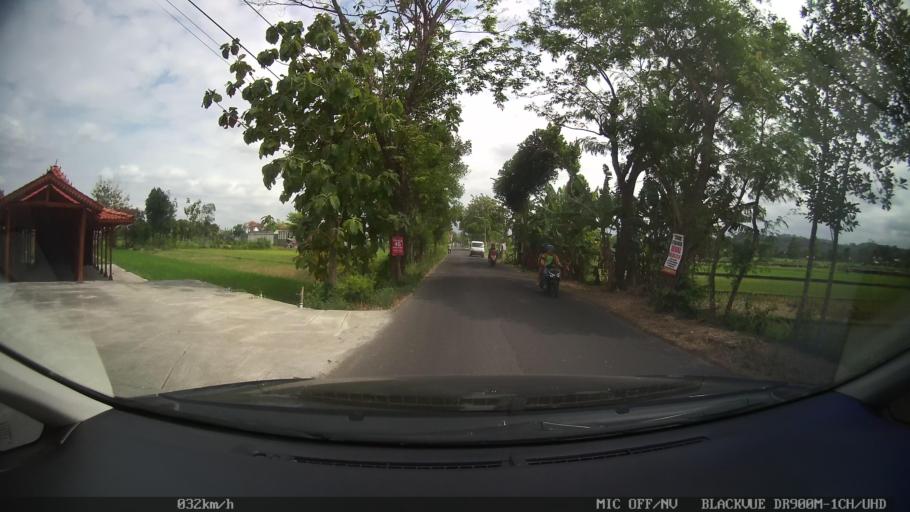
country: ID
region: Central Java
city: Candi Prambanan
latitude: -7.7879
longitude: 110.4813
